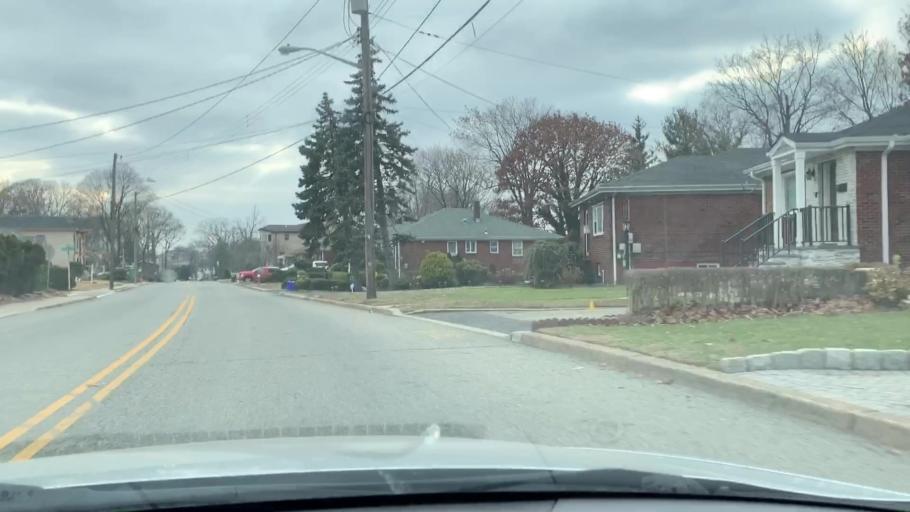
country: US
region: New Jersey
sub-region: Bergen County
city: Edgewater
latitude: 40.8374
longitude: -73.9845
